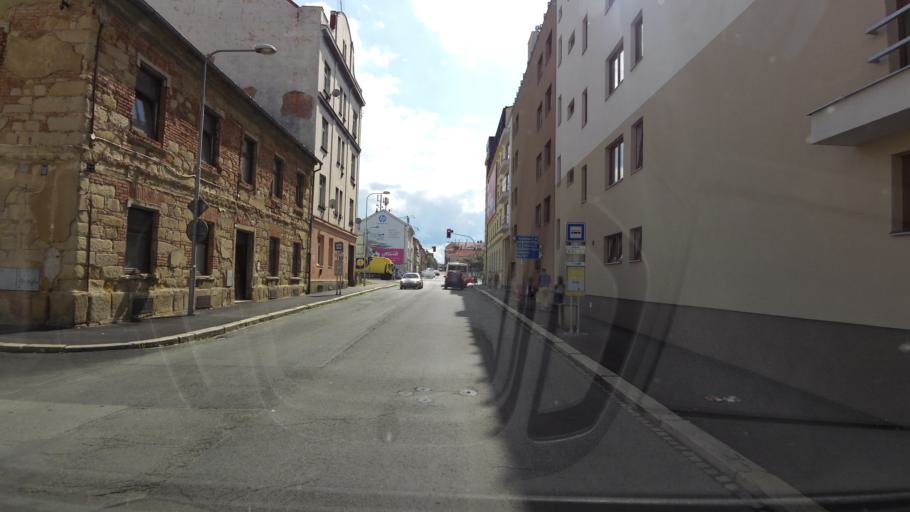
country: CZ
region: Plzensky
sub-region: Okres Plzen-Mesto
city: Pilsen
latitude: 49.7491
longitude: 13.3659
